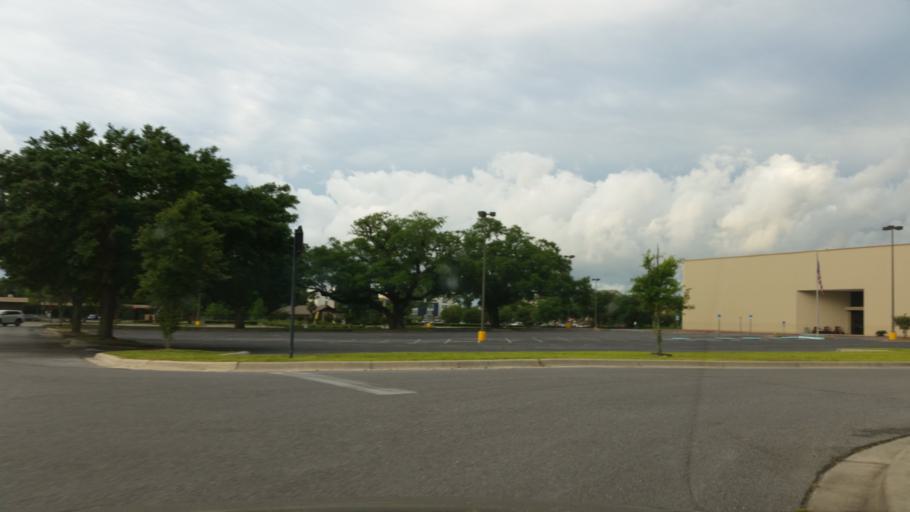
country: US
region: Florida
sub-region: Escambia County
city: Ferry Pass
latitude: 30.4977
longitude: -87.2229
